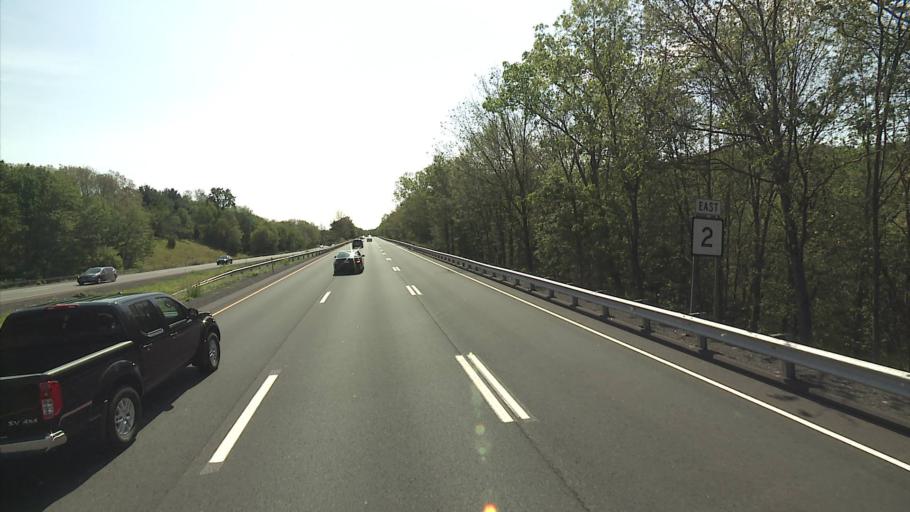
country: US
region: Connecticut
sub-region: Hartford County
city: Terramuggus
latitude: 41.6629
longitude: -72.5264
